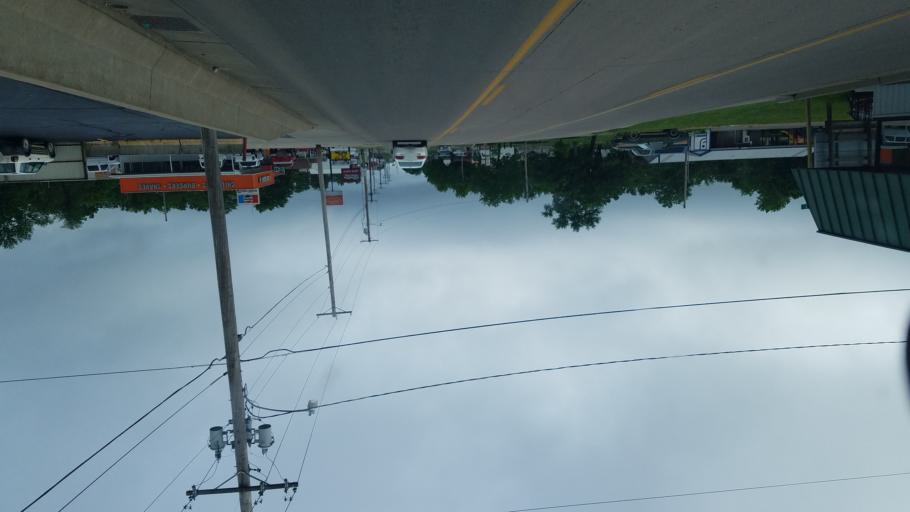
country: US
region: Missouri
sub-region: Miller County
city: Eldon
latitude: 38.3457
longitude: -92.5815
